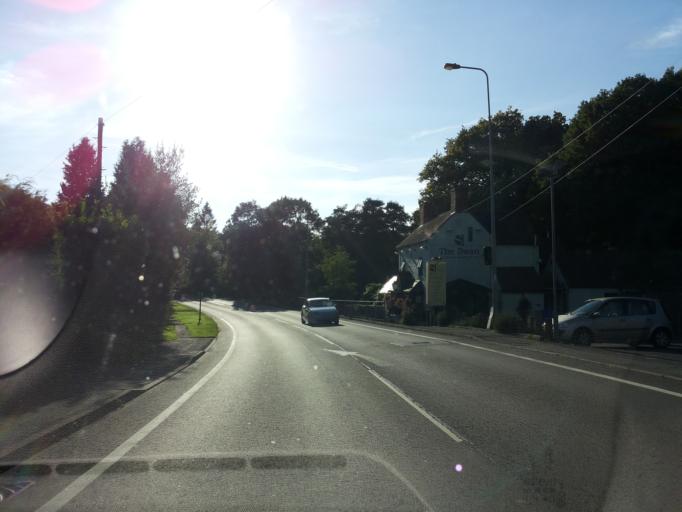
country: GB
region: England
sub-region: Worcestershire
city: Hagley
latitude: 52.4030
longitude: -2.1808
